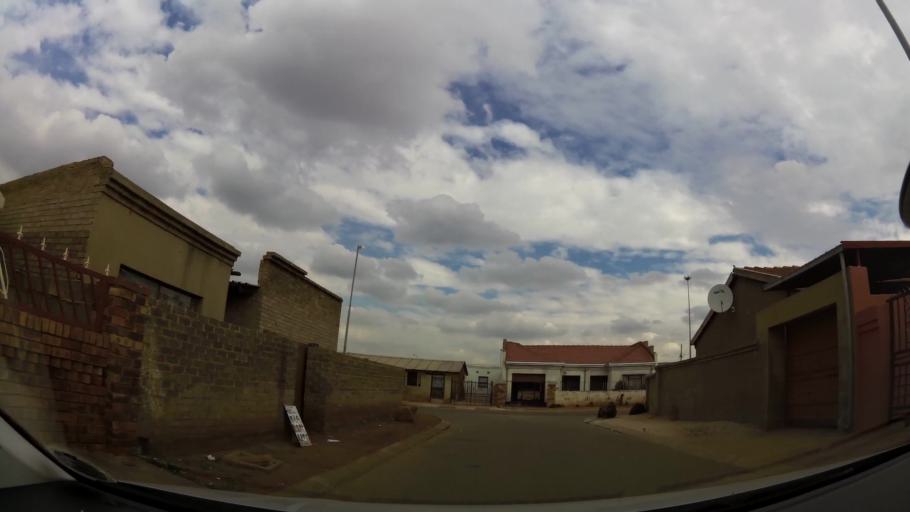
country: ZA
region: Gauteng
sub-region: City of Johannesburg Metropolitan Municipality
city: Soweto
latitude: -26.2746
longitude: 27.8559
